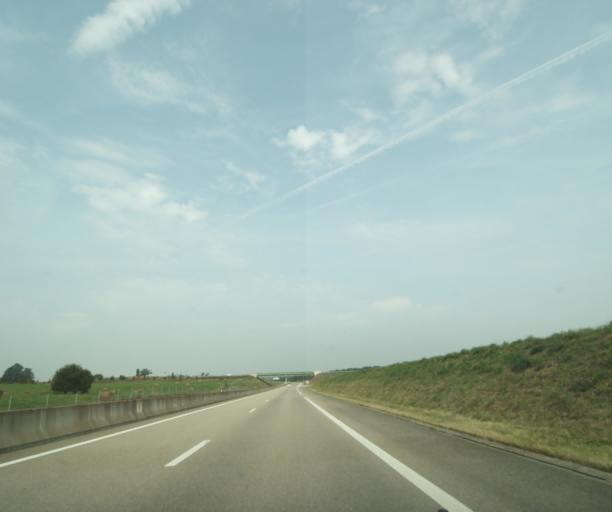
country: FR
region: Lower Normandy
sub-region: Departement du Calvados
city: Falaise
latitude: 48.8522
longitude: -0.1764
